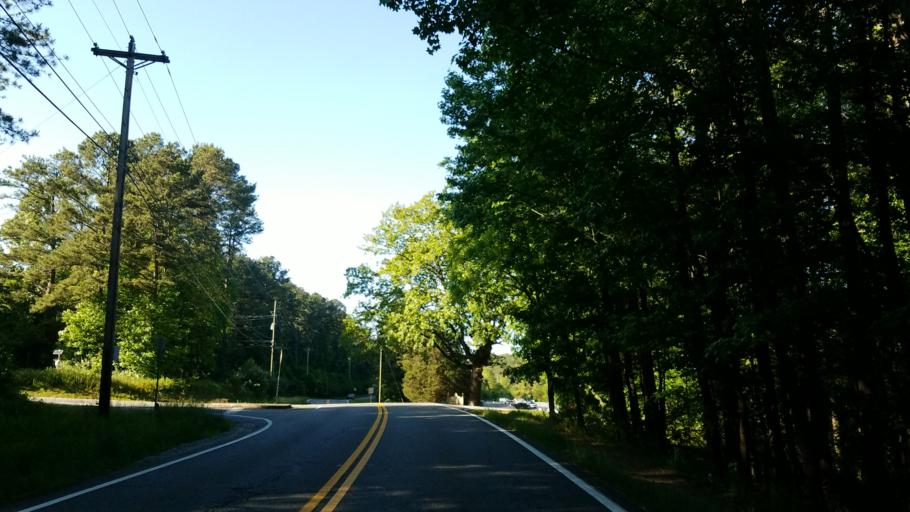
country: US
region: Georgia
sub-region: Cherokee County
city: Holly Springs
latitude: 34.1573
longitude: -84.5832
